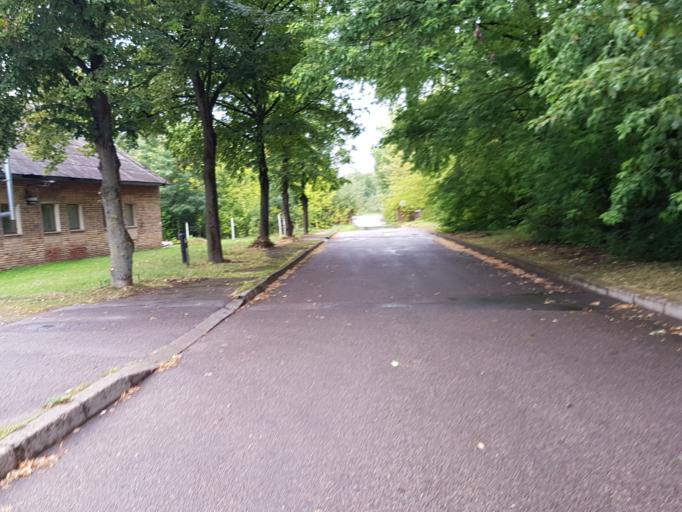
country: LT
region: Vilnius County
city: Lazdynai
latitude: 54.6553
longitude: 25.1945
